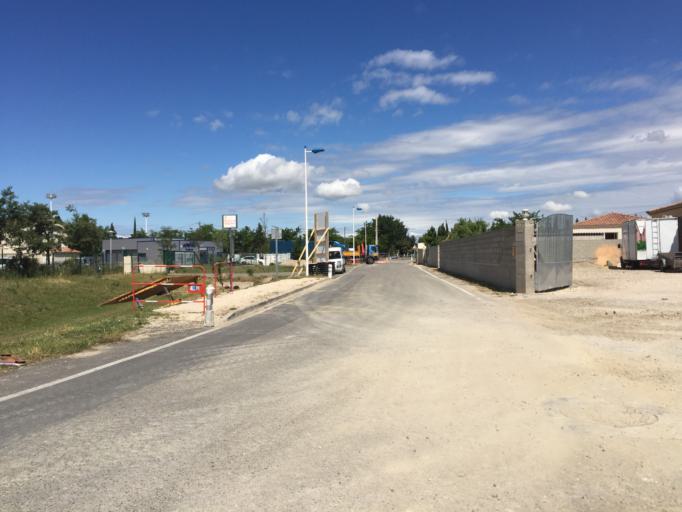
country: FR
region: Provence-Alpes-Cote d'Azur
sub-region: Departement du Vaucluse
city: Vedene
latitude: 43.9935
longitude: 4.8951
